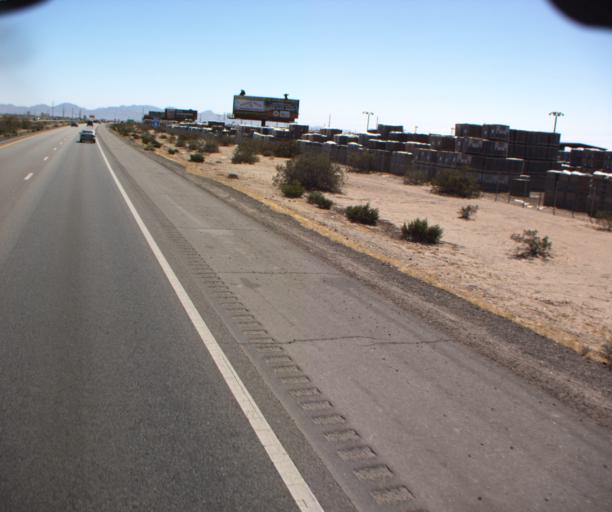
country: US
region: Arizona
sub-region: Yuma County
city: Yuma
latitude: 32.6870
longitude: -114.5721
